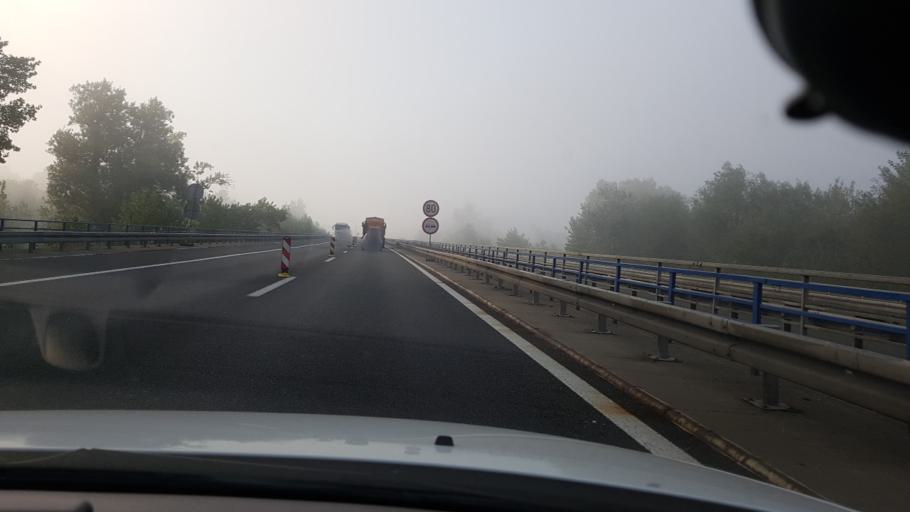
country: HR
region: Zagrebacka
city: Bestovje
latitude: 45.8280
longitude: 15.8195
